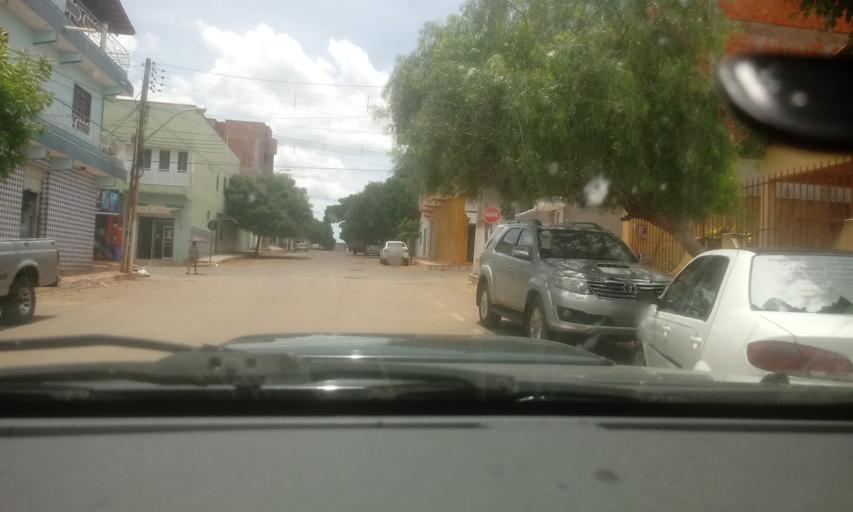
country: BR
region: Bahia
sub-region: Riacho De Santana
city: Riacho de Santana
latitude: -13.6106
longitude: -42.9362
